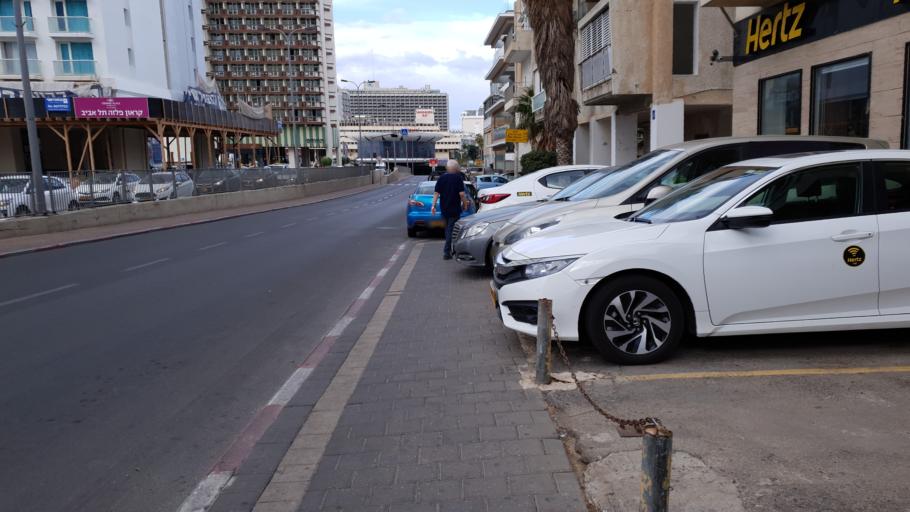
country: IL
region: Tel Aviv
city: Tel Aviv
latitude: 32.0832
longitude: 34.7691
